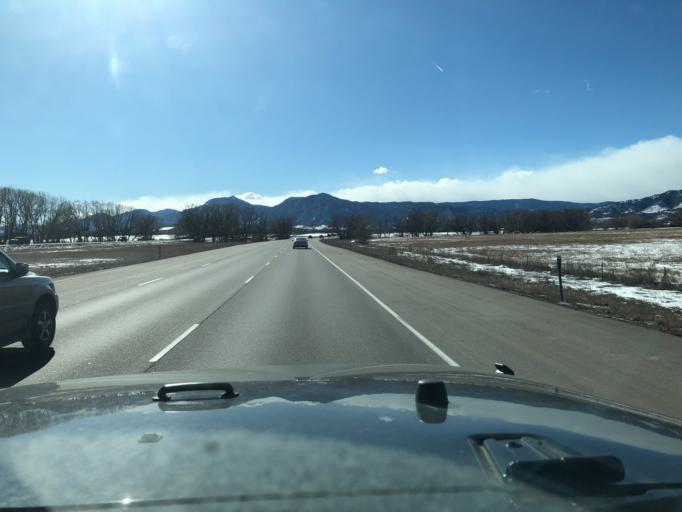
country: US
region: Colorado
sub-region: Boulder County
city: Gunbarrel
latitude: 40.0572
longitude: -105.2269
